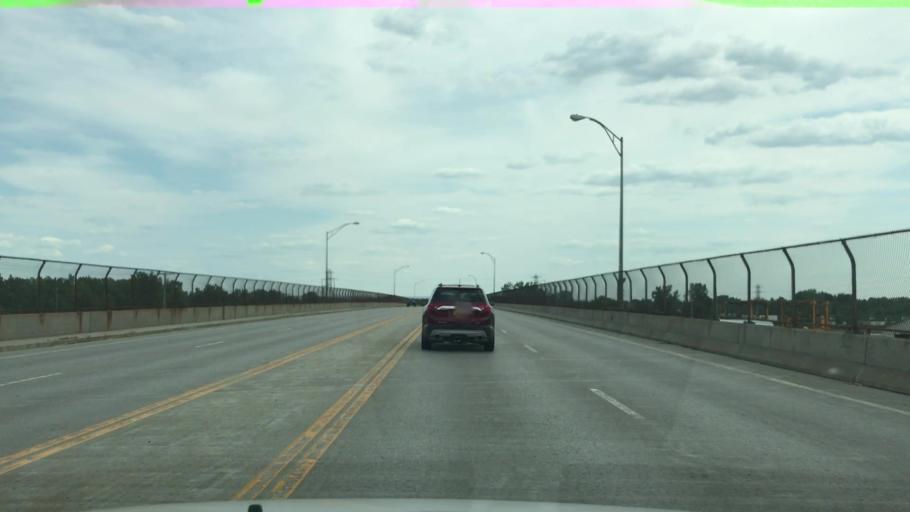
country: US
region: New York
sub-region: Erie County
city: Sloan
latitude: 42.8919
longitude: -78.7847
